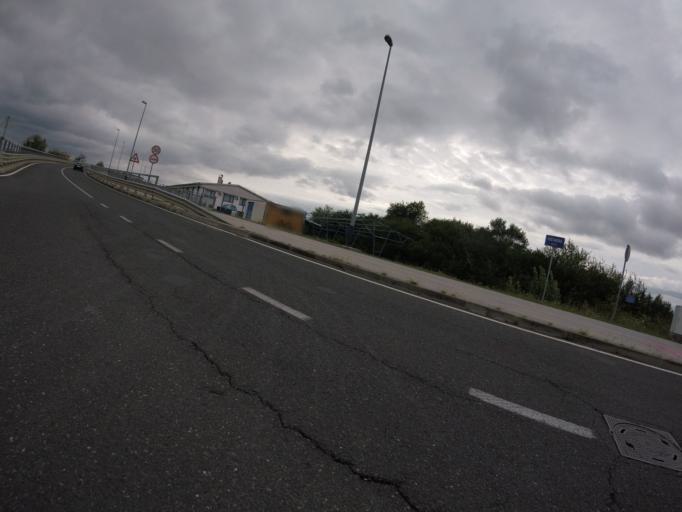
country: HR
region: Zagrebacka
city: Gradici
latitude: 45.7132
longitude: 16.0446
